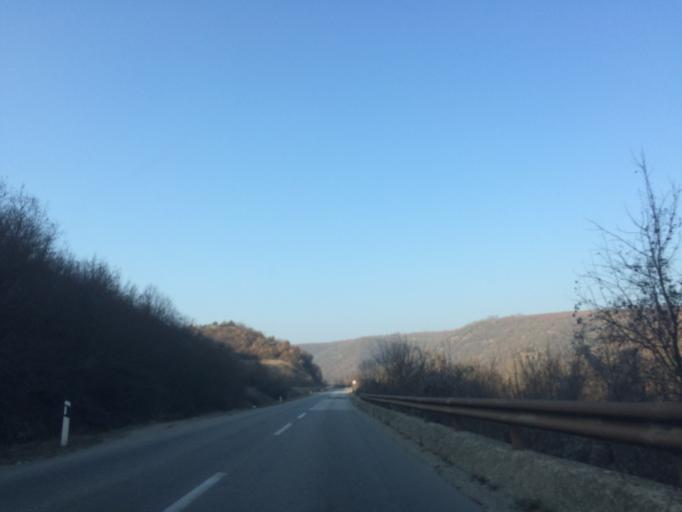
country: XK
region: Pec
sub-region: Komuna e Pejes
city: Kosuriq
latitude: 42.5063
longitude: 20.5352
